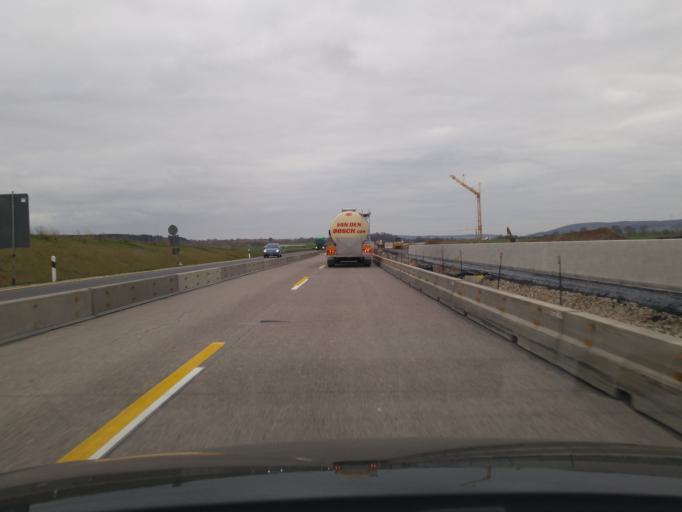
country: DE
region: Lower Saxony
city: Seesen
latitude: 51.9401
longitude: 10.1453
